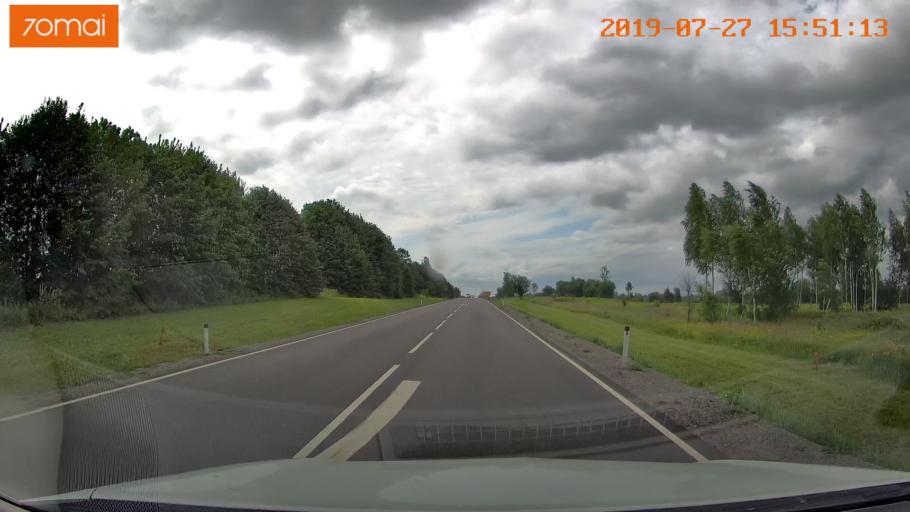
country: RU
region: Kaliningrad
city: Chernyakhovsk
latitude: 54.6023
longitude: 21.9859
